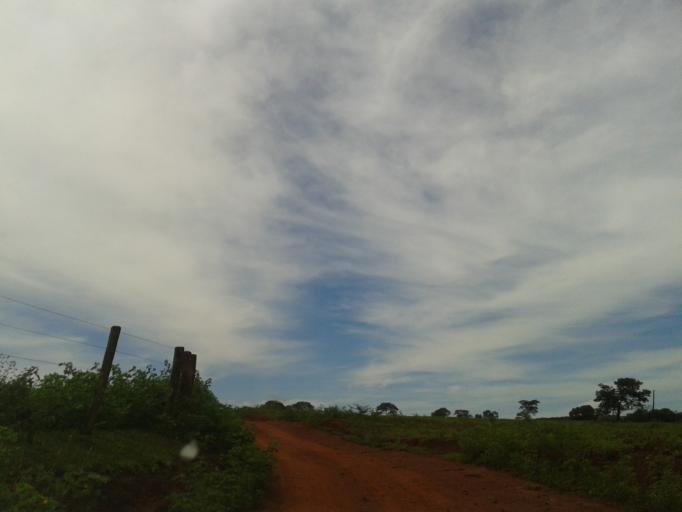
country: BR
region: Minas Gerais
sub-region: Capinopolis
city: Capinopolis
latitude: -18.7837
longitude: -49.8024
